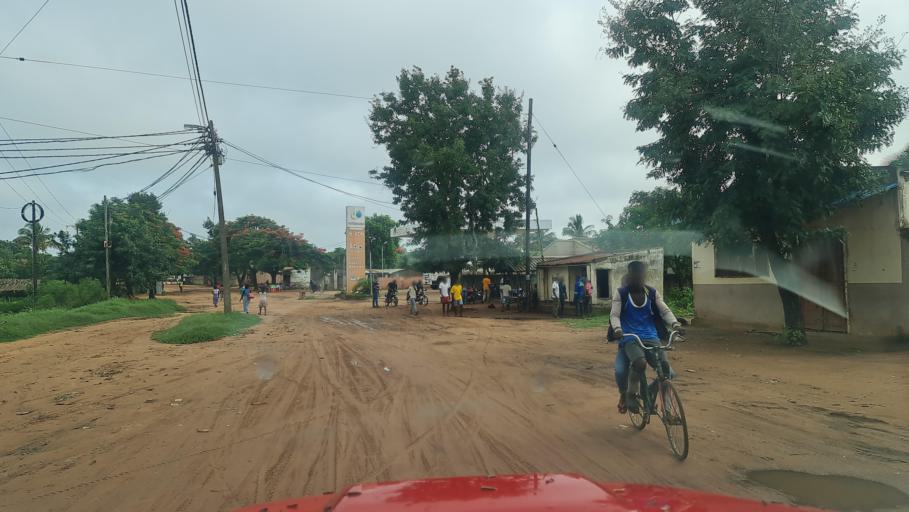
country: MW
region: Southern Region
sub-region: Nsanje District
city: Nsanje
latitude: -17.3260
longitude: 35.5913
